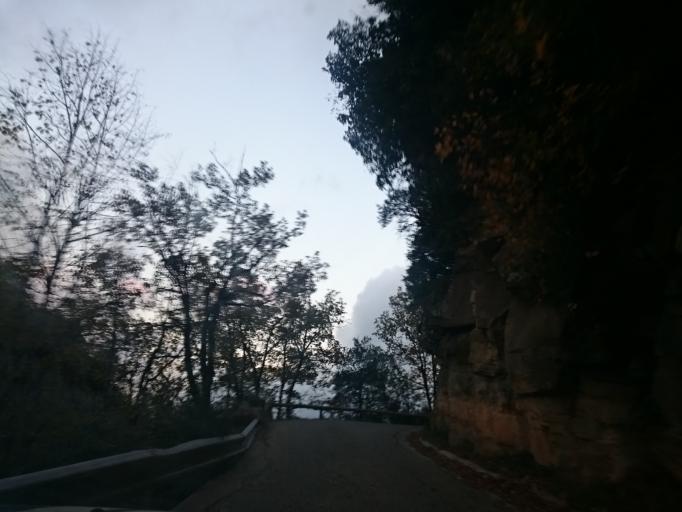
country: ES
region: Catalonia
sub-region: Provincia de Barcelona
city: Tavertet
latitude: 42.0185
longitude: 2.4665
